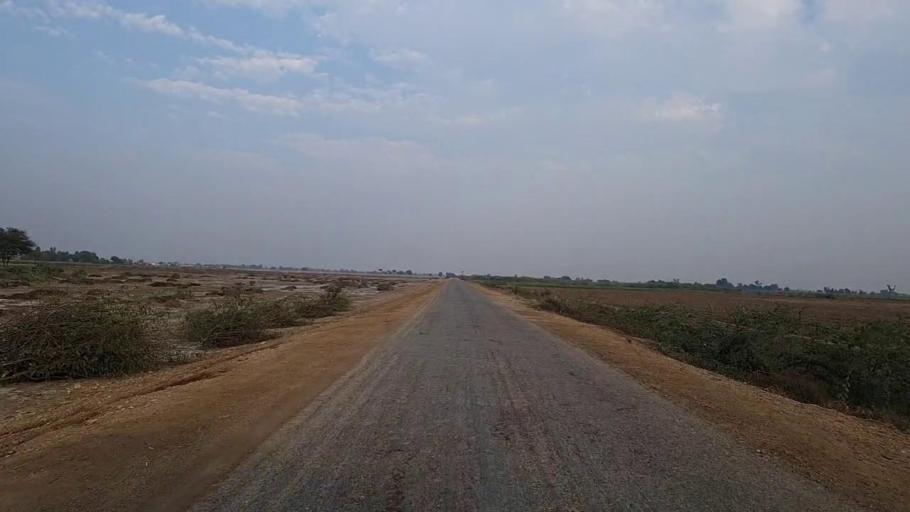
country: PK
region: Sindh
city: Samaro
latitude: 25.3836
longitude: 69.3552
